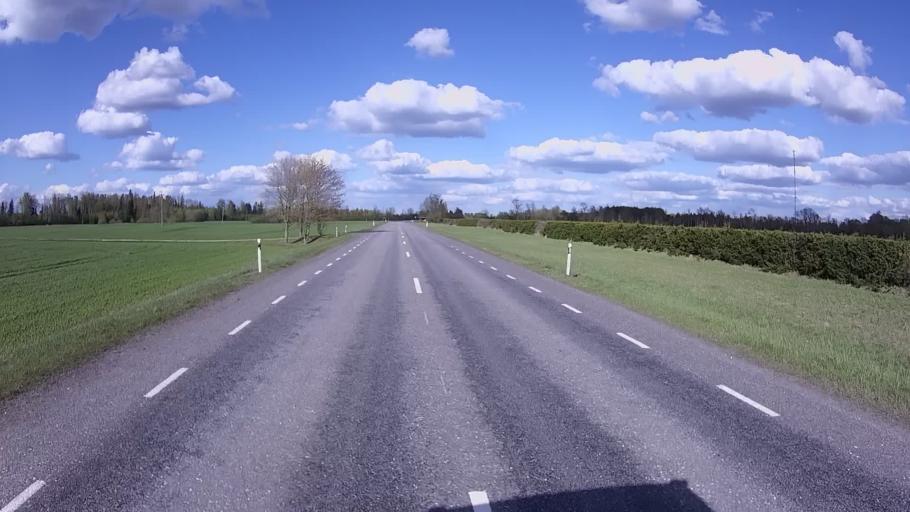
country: EE
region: Jogevamaa
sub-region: Poltsamaa linn
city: Poltsamaa
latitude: 58.6981
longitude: 26.1409
